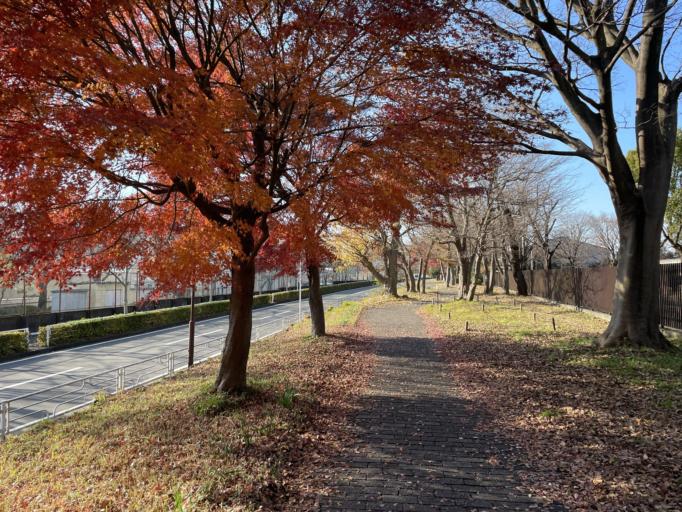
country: JP
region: Saitama
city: Asaka
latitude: 35.7780
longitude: 139.5918
